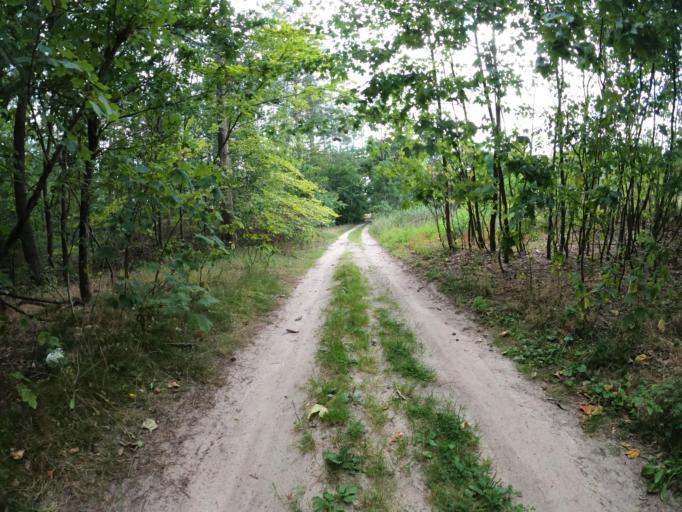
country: PL
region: West Pomeranian Voivodeship
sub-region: Powiat lobeski
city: Lobez
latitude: 53.7521
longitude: 15.6435
